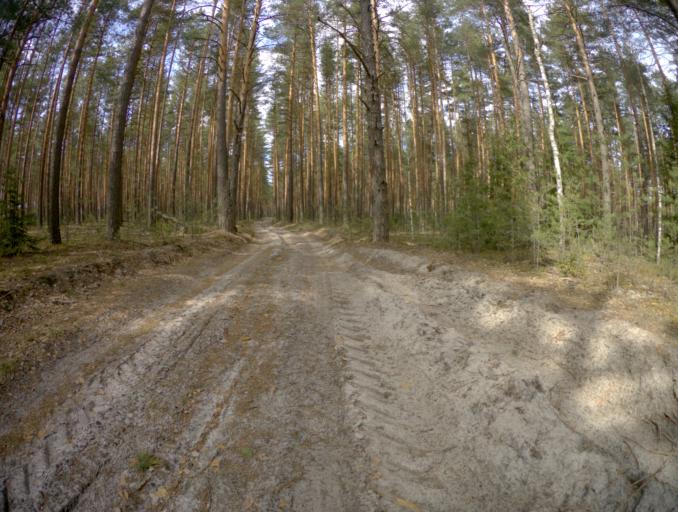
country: RU
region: Vladimir
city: Urshel'skiy
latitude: 55.8707
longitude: 40.1911
